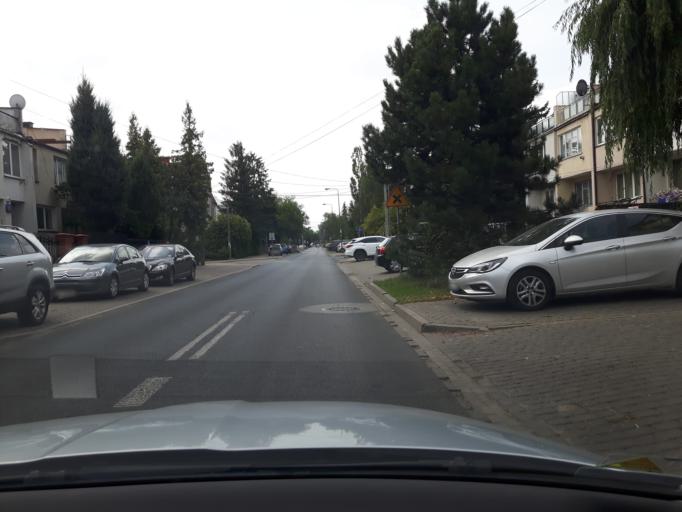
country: PL
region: Masovian Voivodeship
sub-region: Warszawa
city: Mokotow
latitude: 52.1917
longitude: 21.0670
